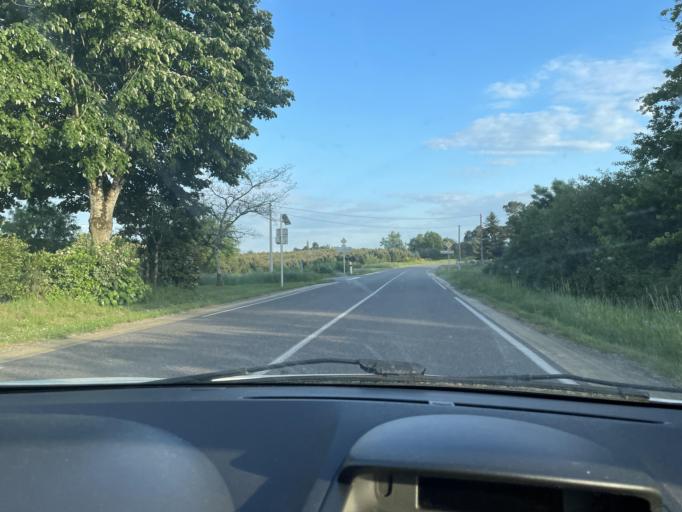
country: FR
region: Aquitaine
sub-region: Departement de la Gironde
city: Grignols
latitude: 44.4172
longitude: -0.0794
